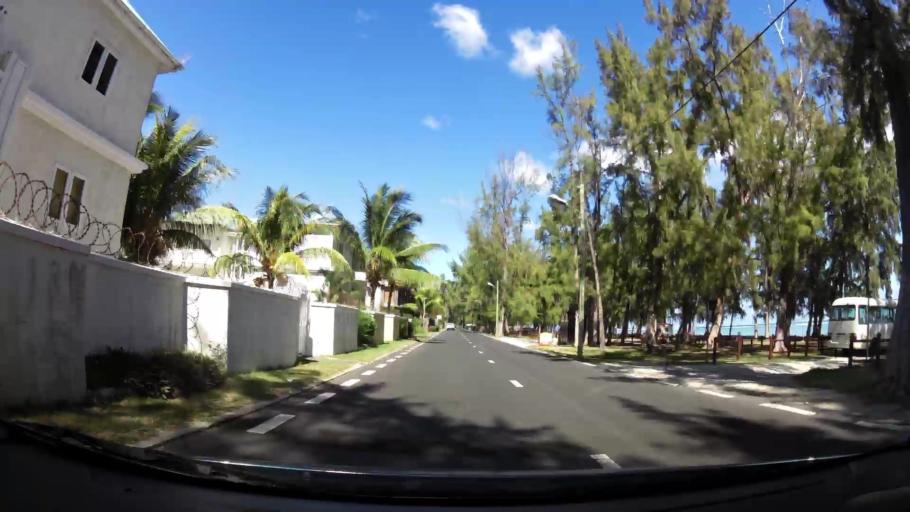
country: MU
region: Black River
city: Flic en Flac
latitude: -20.2868
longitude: 57.3641
